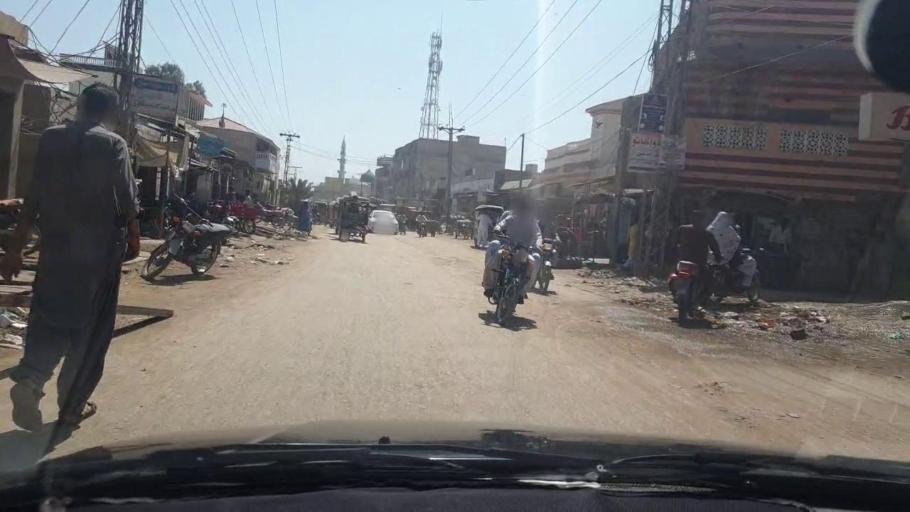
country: PK
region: Sindh
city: Tando Allahyar
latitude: 25.4584
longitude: 68.7179
